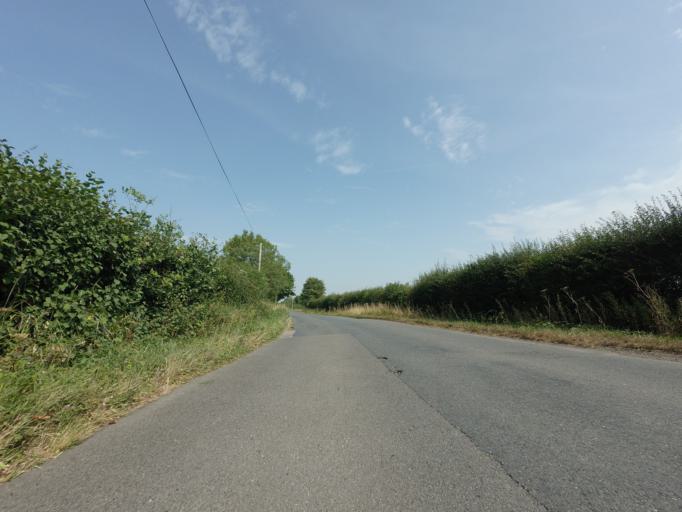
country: GB
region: England
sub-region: Kent
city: Headcorn
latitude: 51.1590
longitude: 0.6067
